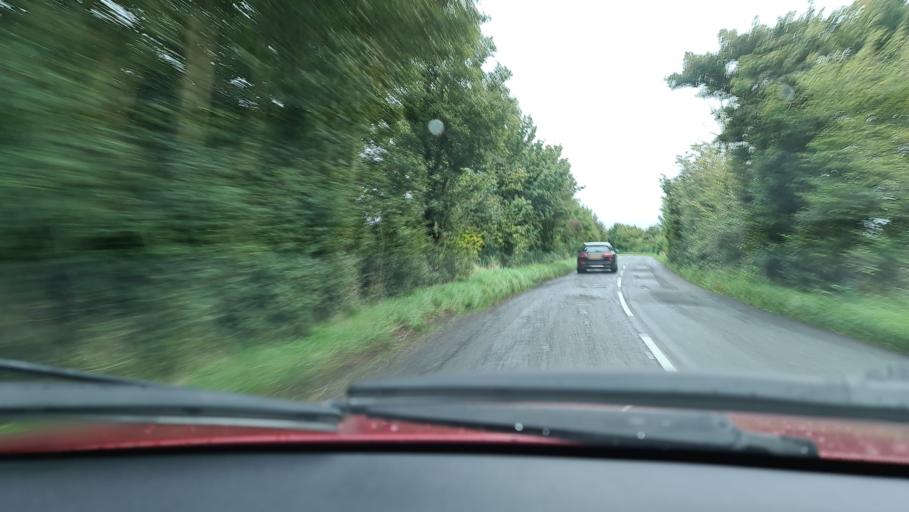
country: GB
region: England
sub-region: Oxfordshire
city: Bicester
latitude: 51.9425
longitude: -1.2068
